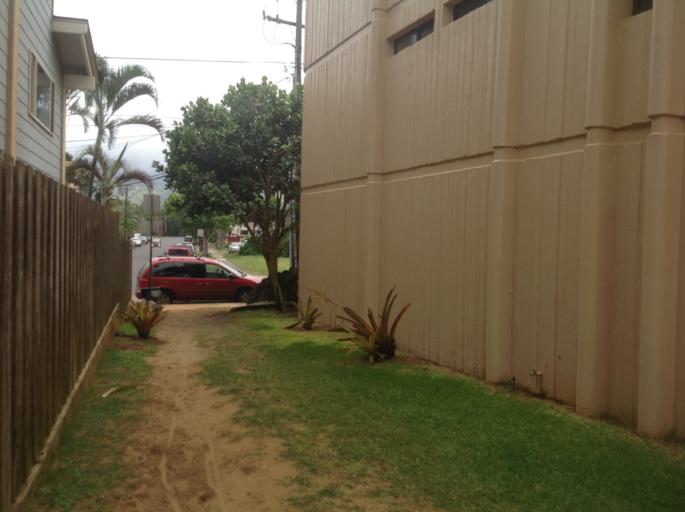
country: US
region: Hawaii
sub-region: Honolulu County
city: Waialua
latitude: 21.5839
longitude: -158.1376
